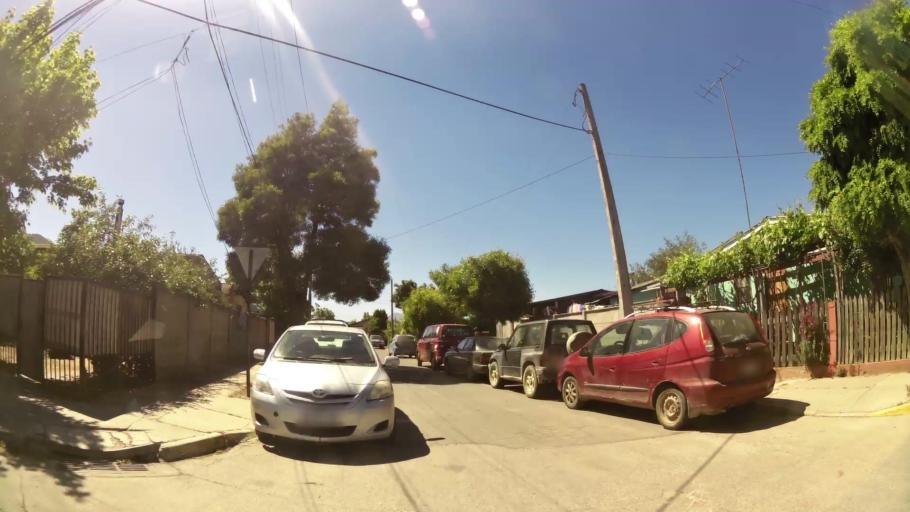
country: CL
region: Valparaiso
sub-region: Provincia de Marga Marga
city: Quilpue
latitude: -33.3226
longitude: -71.4040
